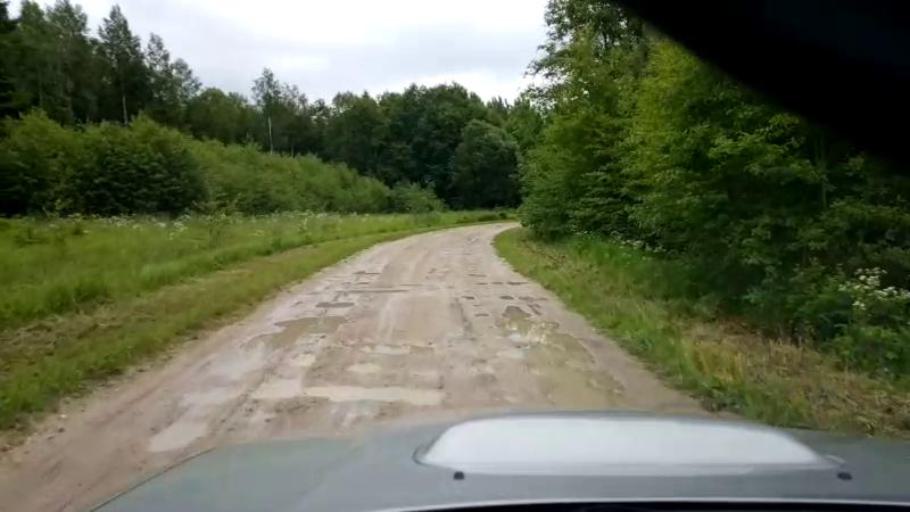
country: EE
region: Paernumaa
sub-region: Halinga vald
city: Parnu-Jaagupi
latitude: 58.5486
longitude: 24.5769
